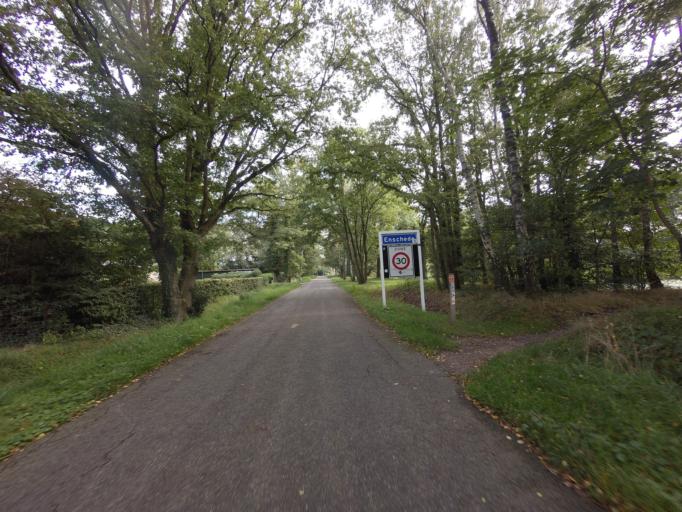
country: NL
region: Overijssel
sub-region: Gemeente Enschede
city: Enschede
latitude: 52.2426
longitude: 6.8715
